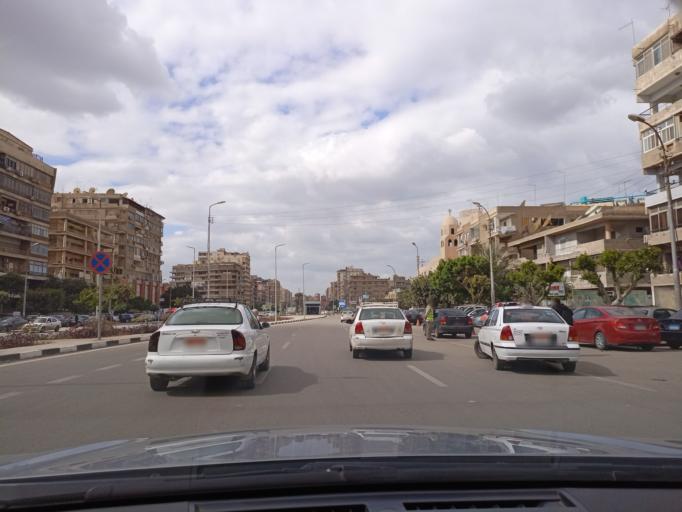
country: EG
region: Muhafazat al Qahirah
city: Cairo
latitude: 30.1072
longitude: 31.3403
